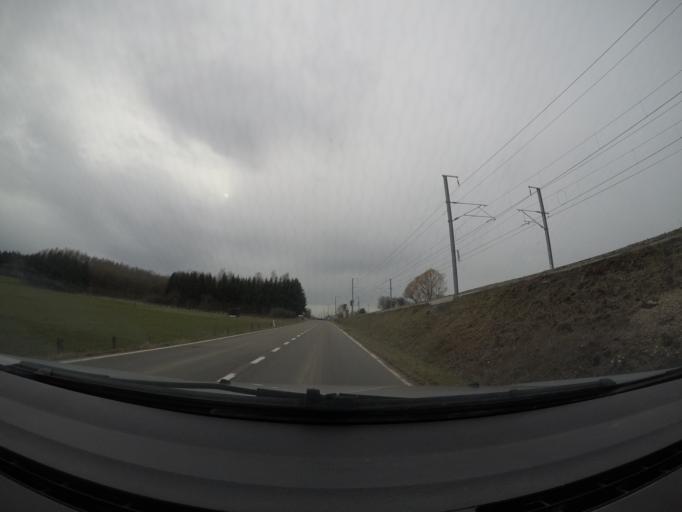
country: BE
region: Wallonia
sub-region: Province du Luxembourg
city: Habay-la-Vieille
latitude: 49.7201
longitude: 5.6149
